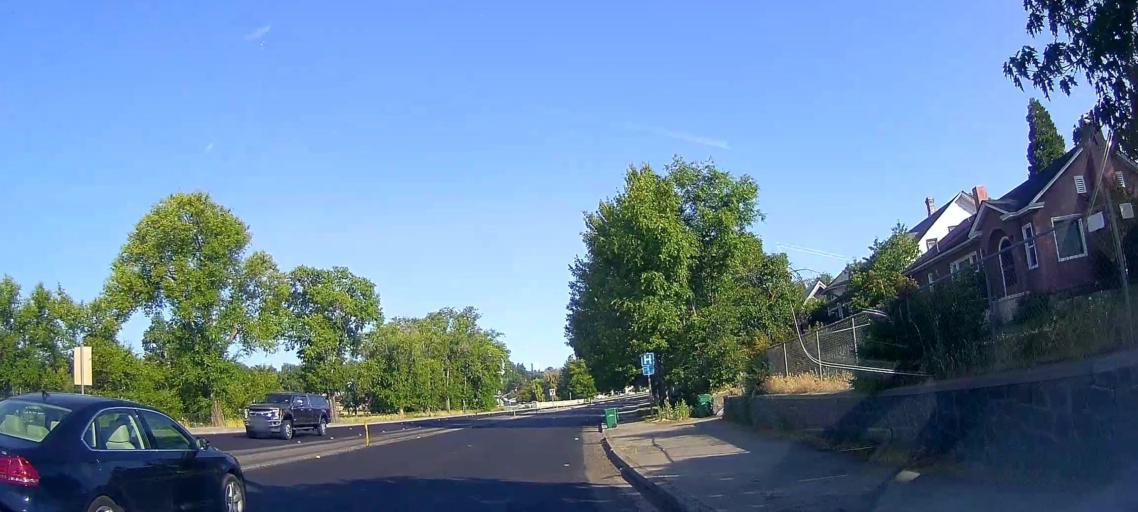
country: US
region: Oregon
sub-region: Klamath County
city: Klamath Falls
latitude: 42.2324
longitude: -121.7744
